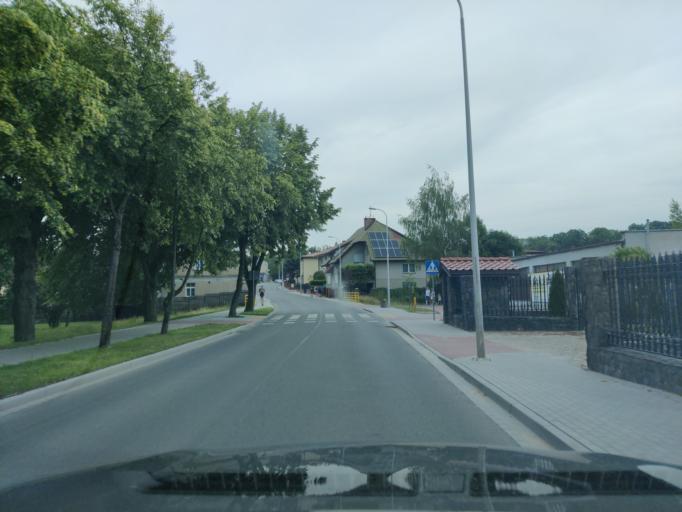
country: PL
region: Warmian-Masurian Voivodeship
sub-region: Powiat dzialdowski
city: Dzialdowo
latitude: 53.2351
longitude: 20.1842
